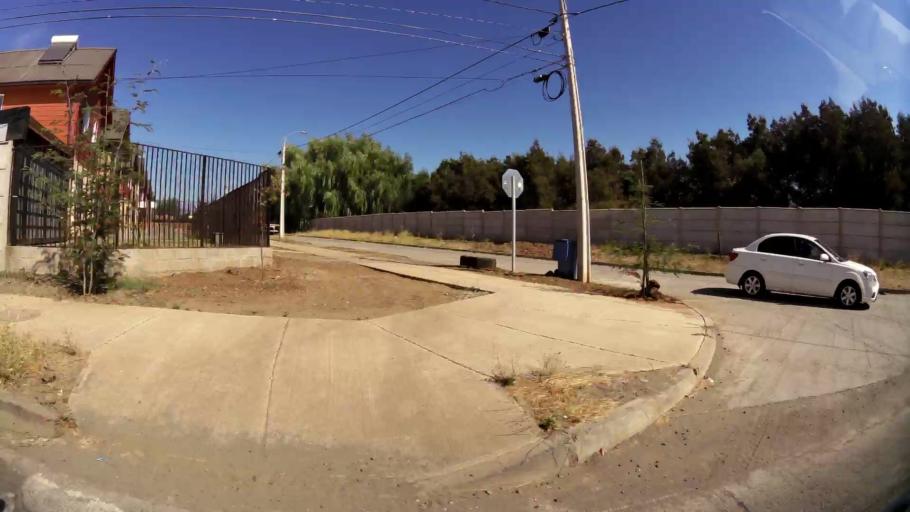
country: CL
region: Maule
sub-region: Provincia de Talca
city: Talca
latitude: -35.4152
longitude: -71.6165
